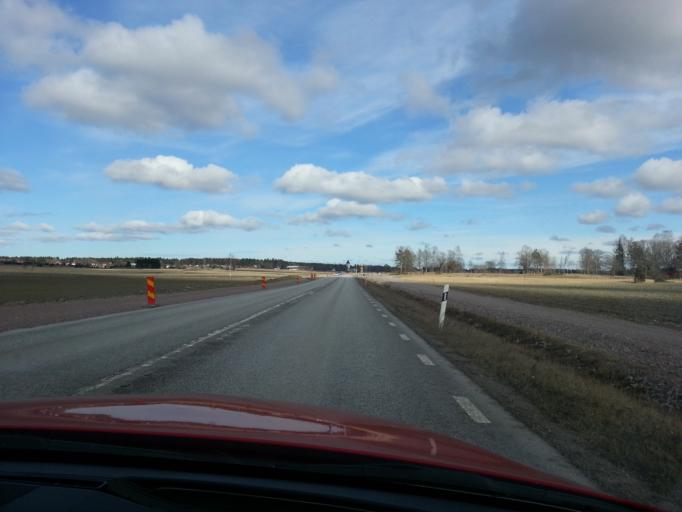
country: SE
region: Uppsala
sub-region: Osthammars Kommun
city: Gimo
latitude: 60.0487
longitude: 18.0495
